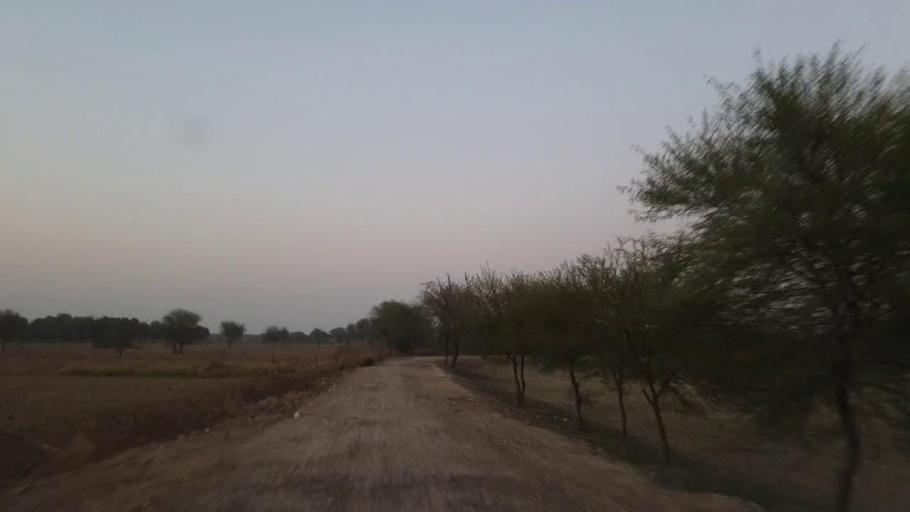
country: PK
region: Sindh
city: Bandhi
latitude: 26.6262
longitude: 68.3954
